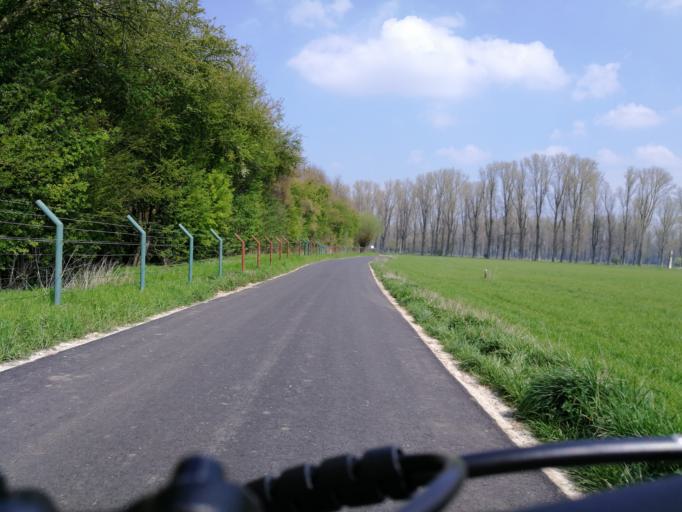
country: DE
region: North Rhine-Westphalia
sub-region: Regierungsbezirk Dusseldorf
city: Dormagen
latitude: 51.1484
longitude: 6.8307
